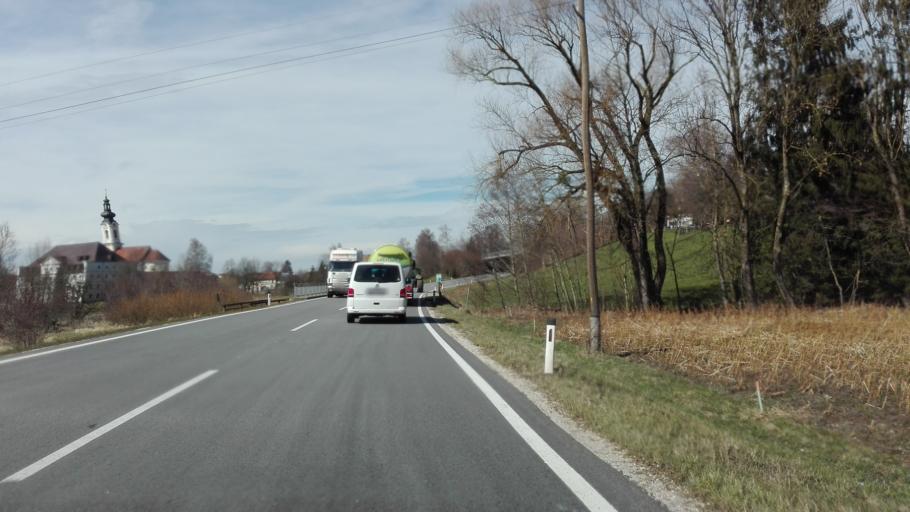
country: AT
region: Upper Austria
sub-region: Politischer Bezirk Ried im Innkreis
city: Ried im Innkreis
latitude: 48.3136
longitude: 13.6344
